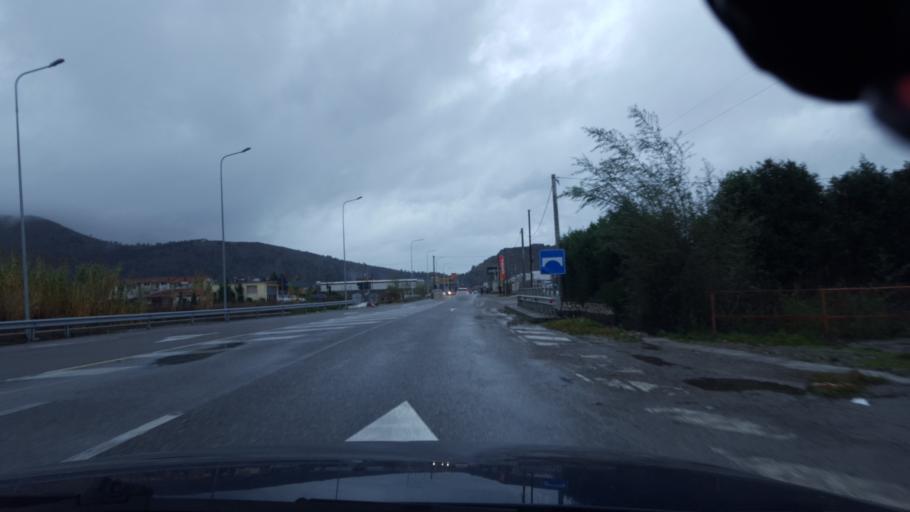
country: AL
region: Shkoder
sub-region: Rrethi i Malesia e Madhe
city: Kuc
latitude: 42.0323
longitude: 19.5030
